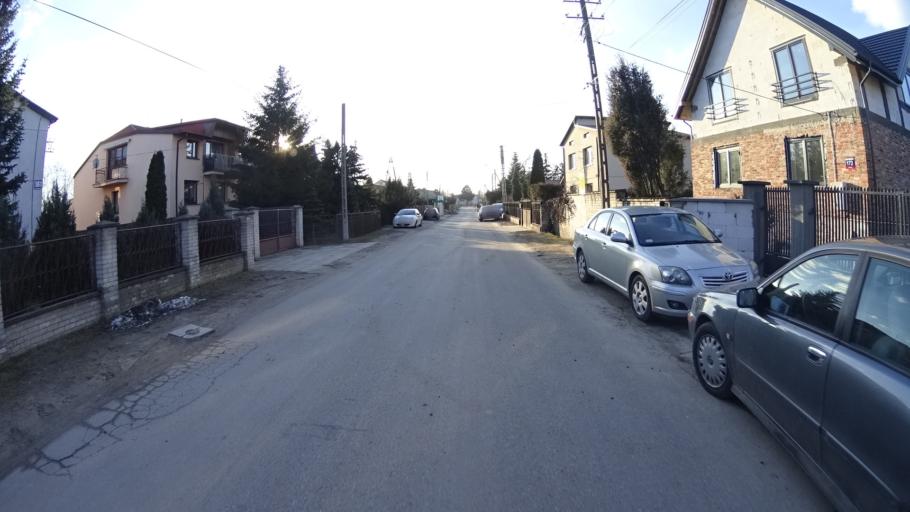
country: PL
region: Masovian Voivodeship
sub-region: Powiat warszawski zachodni
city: Truskaw
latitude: 52.2595
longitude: 20.7546
